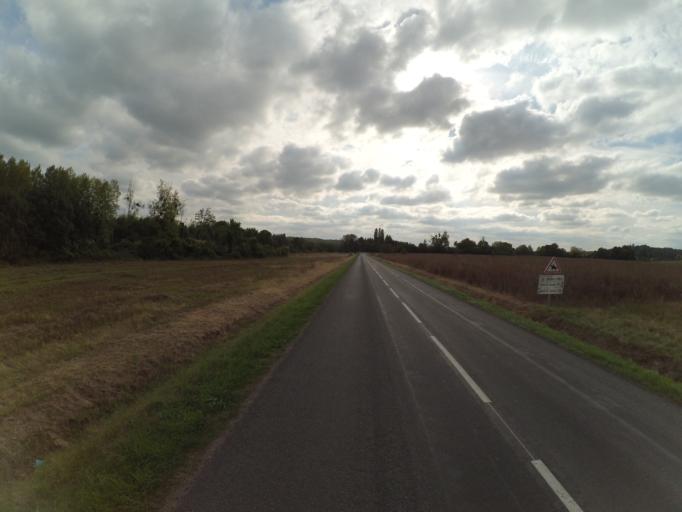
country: FR
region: Centre
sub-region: Departement d'Indre-et-Loire
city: Vernou-sur-Brenne
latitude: 47.4467
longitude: 0.8654
